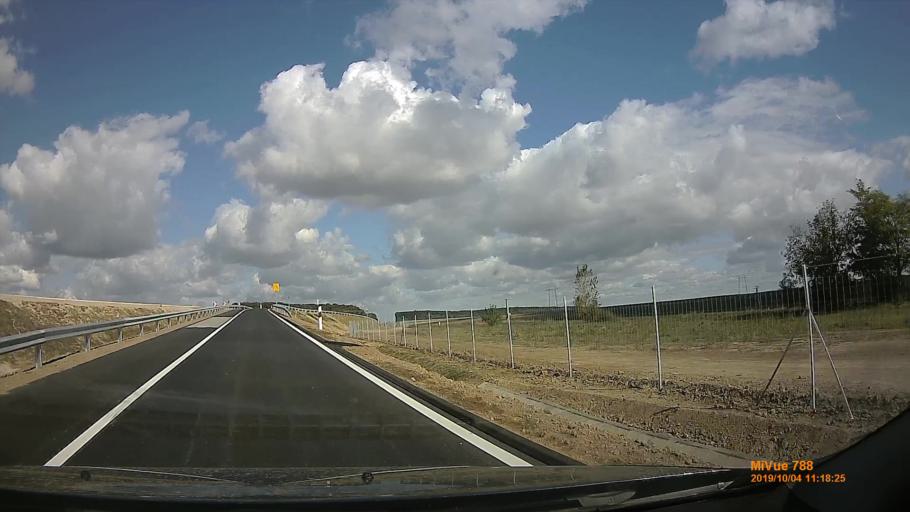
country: HU
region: Somogy
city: Kaposvar
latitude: 46.4714
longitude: 17.8026
